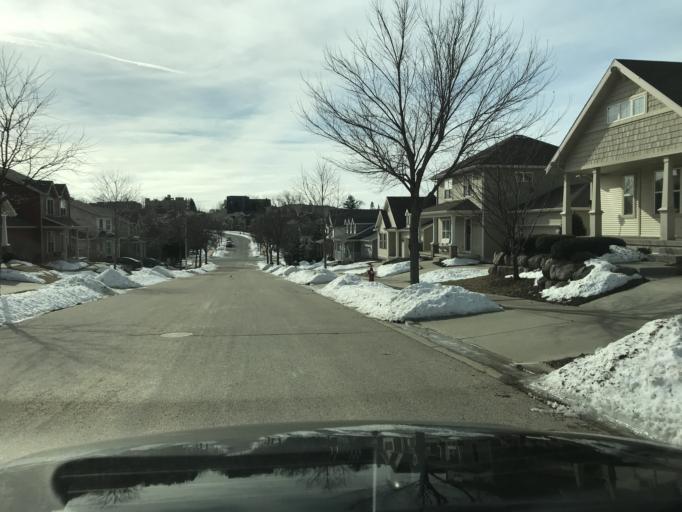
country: US
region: Wisconsin
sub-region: Dane County
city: Monona
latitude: 43.0914
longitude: -89.2801
